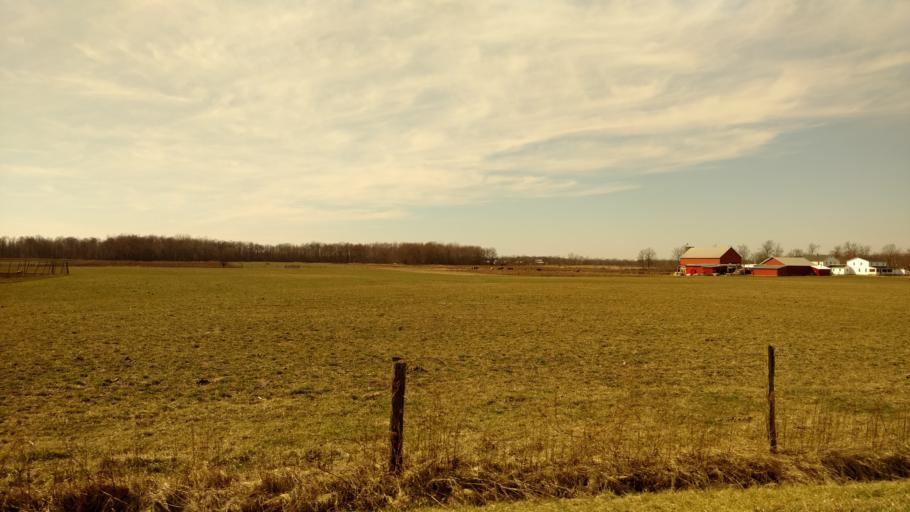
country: US
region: Ohio
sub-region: Hardin County
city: Kenton
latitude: 40.5980
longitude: -83.5041
